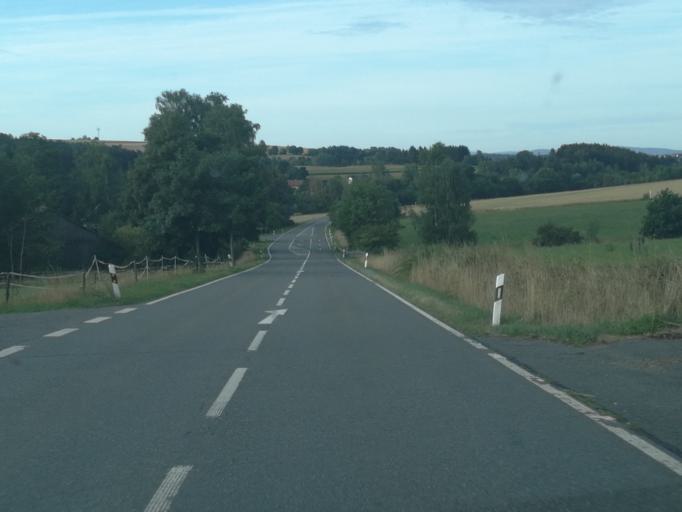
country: DE
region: Bavaria
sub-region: Upper Franconia
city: Regnitzlosau
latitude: 50.3237
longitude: 12.0653
